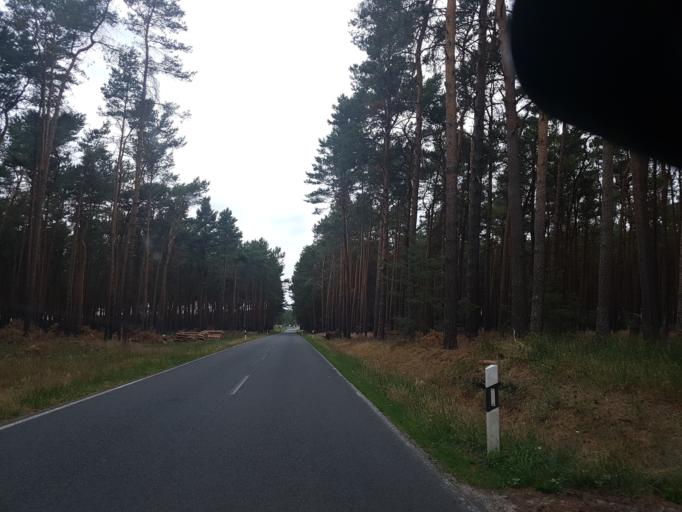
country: DE
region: Brandenburg
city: Linthe
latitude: 52.0849
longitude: 12.8003
